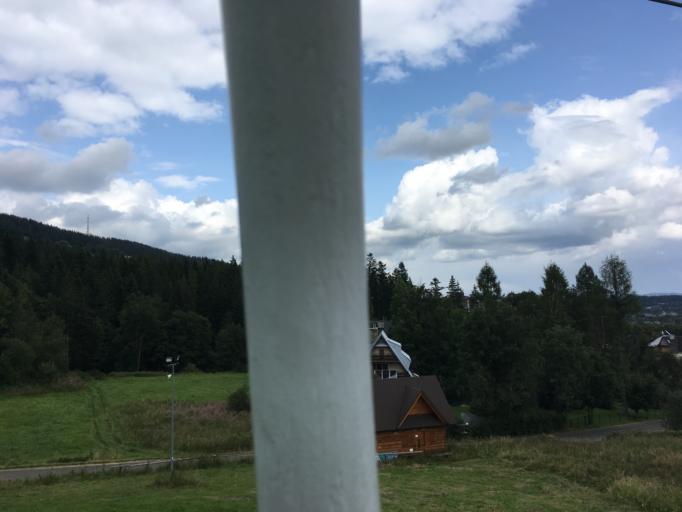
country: PL
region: Lesser Poland Voivodeship
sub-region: Powiat tatrzanski
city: Zakopane
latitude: 49.2916
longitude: 19.9208
